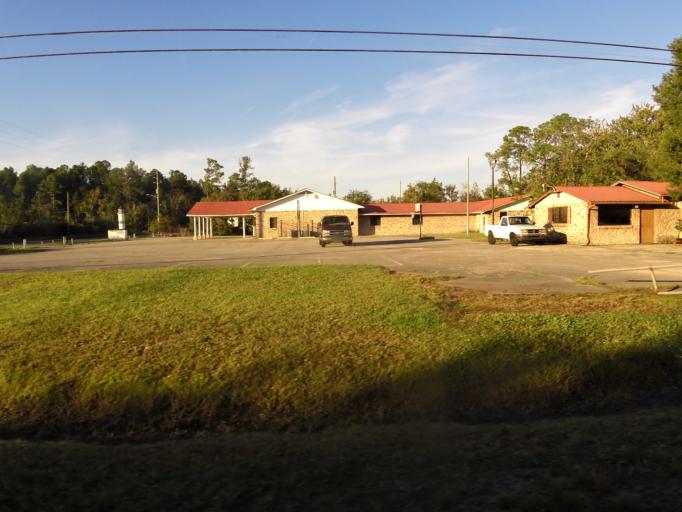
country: US
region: Florida
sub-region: Duval County
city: Jacksonville
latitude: 30.3531
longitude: -81.7643
